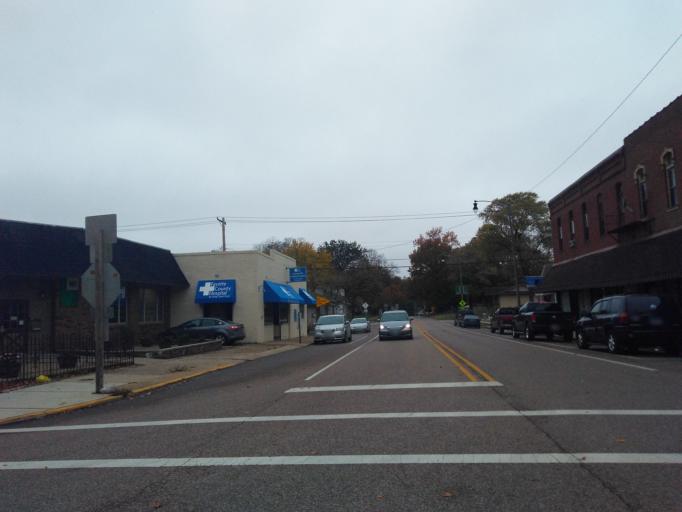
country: US
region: Illinois
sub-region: Bond County
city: Greenville
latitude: 38.8927
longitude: -89.4135
